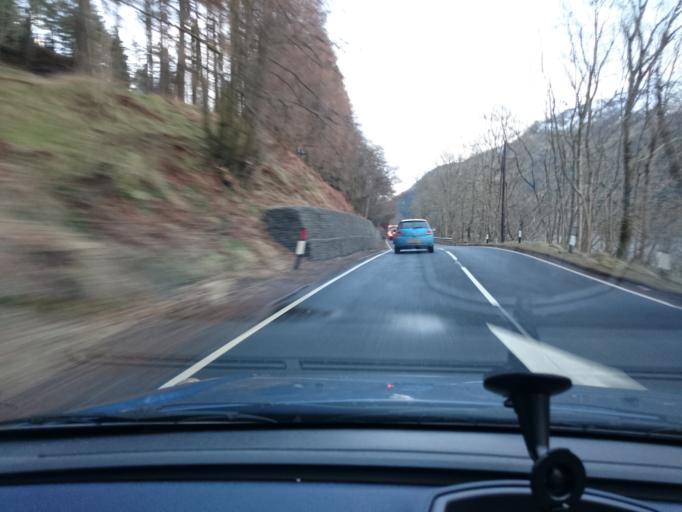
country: GB
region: Scotland
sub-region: Stirling
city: Callander
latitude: 56.3039
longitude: -4.3183
